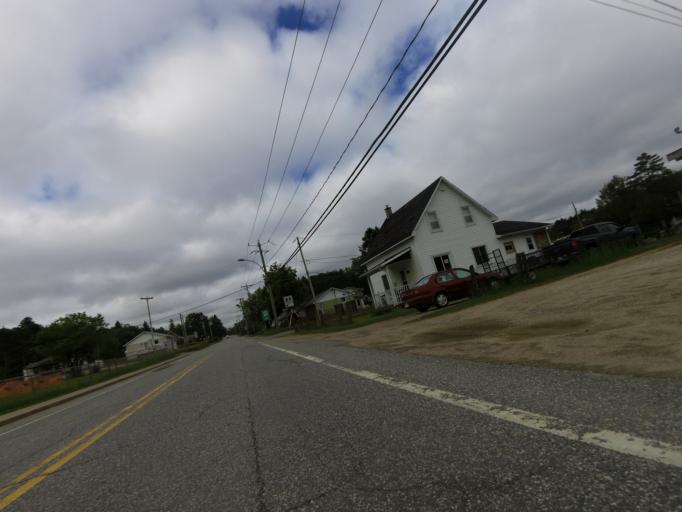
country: CA
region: Quebec
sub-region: Outaouais
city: Shawville
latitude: 45.8452
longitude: -76.4337
